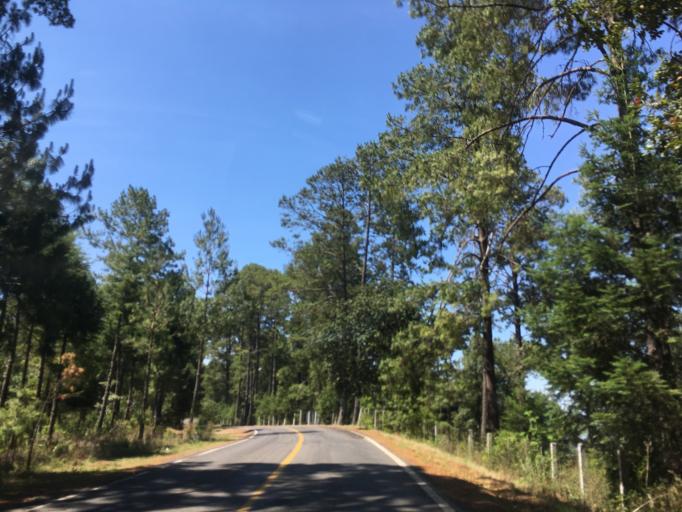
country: MX
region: Michoacan
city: Tzitzio
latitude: 19.6231
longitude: -100.7754
